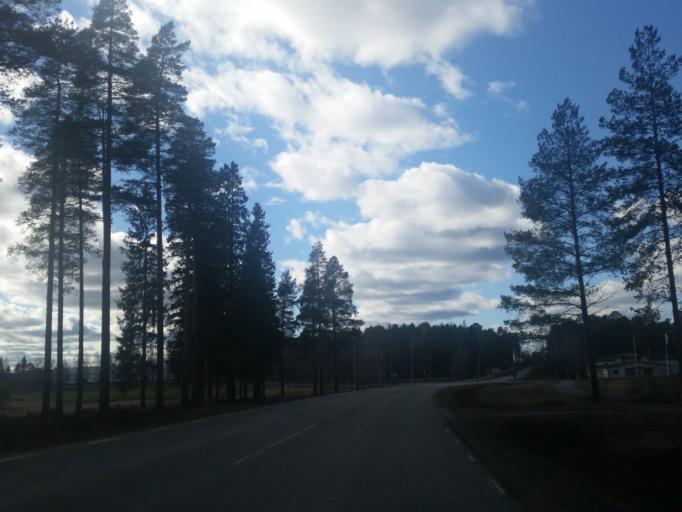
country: SE
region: Vaesterbotten
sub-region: Robertsfors Kommun
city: Robertsfors
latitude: 64.1852
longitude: 20.8660
